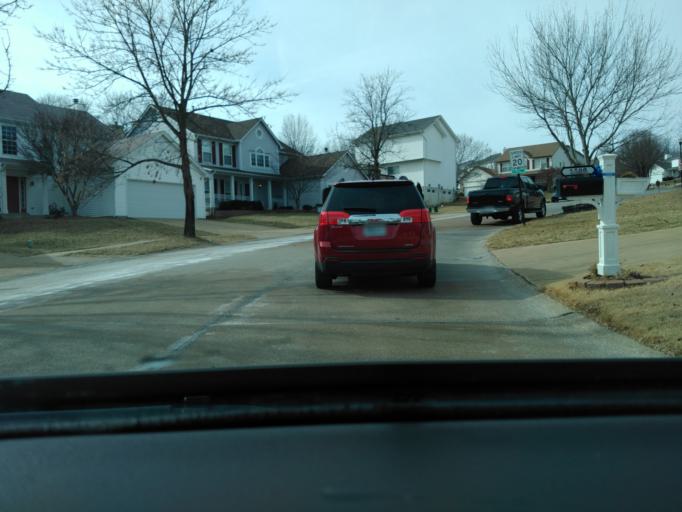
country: US
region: Missouri
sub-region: Saint Louis County
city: Valley Park
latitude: 38.5509
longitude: -90.5120
